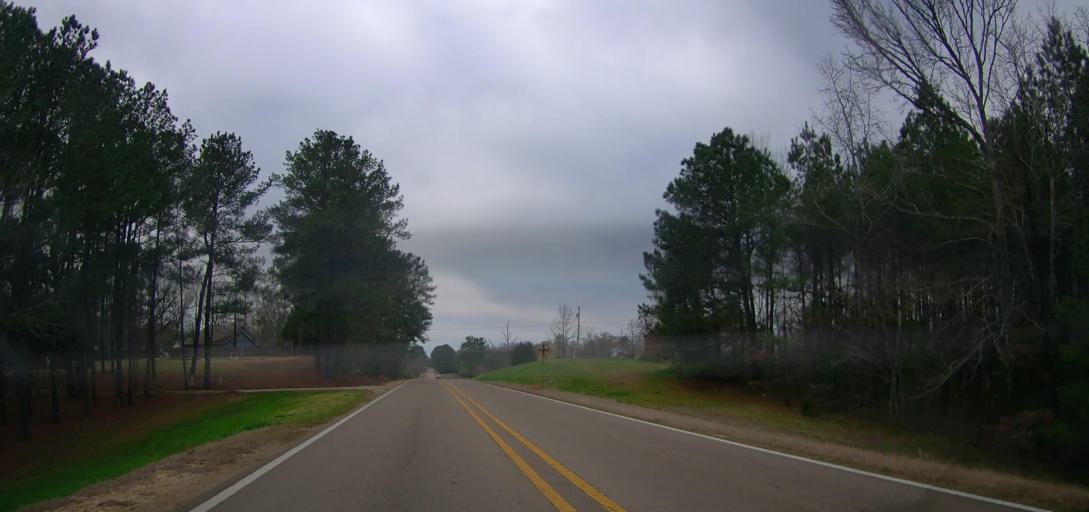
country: US
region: Mississippi
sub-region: Itawamba County
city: Mantachie
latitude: 34.2642
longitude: -88.5414
